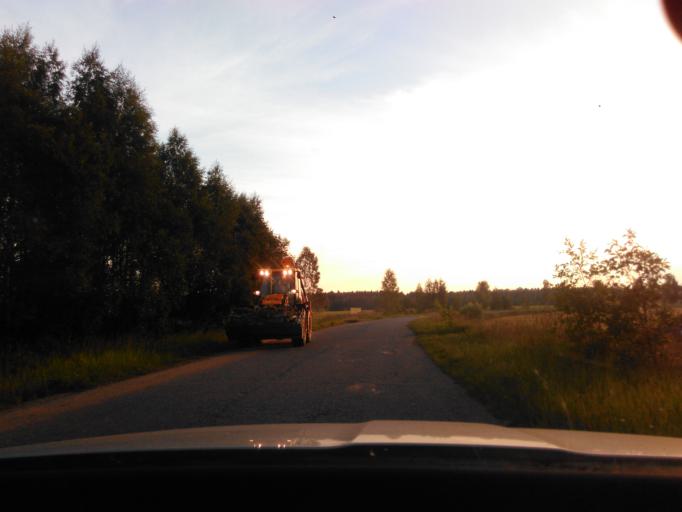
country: RU
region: Tverskaya
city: Zavidovo
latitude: 56.5965
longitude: 36.6050
